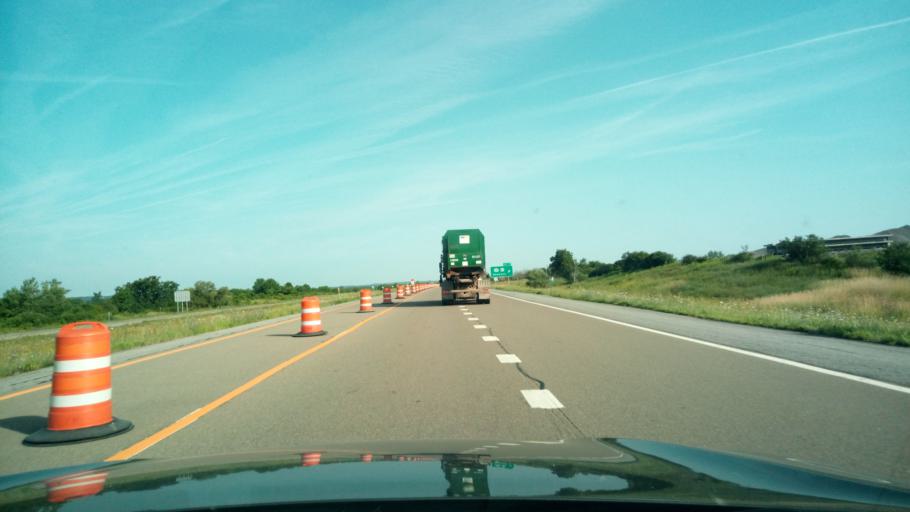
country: US
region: New York
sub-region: Livingston County
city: Mount Morris
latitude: 42.7305
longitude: -77.8326
